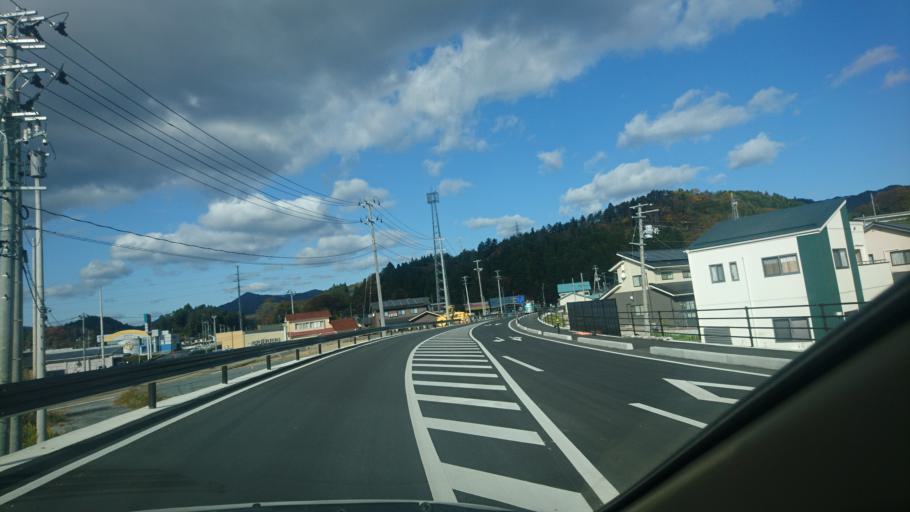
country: JP
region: Iwate
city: Ofunato
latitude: 38.9185
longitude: 141.5866
